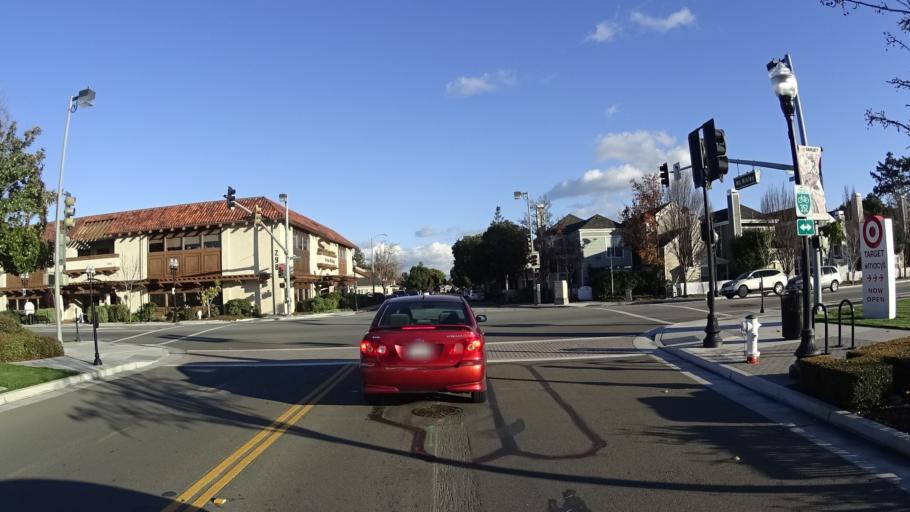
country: US
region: California
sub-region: Santa Clara County
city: Sunnyvale
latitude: 37.3741
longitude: -122.0304
